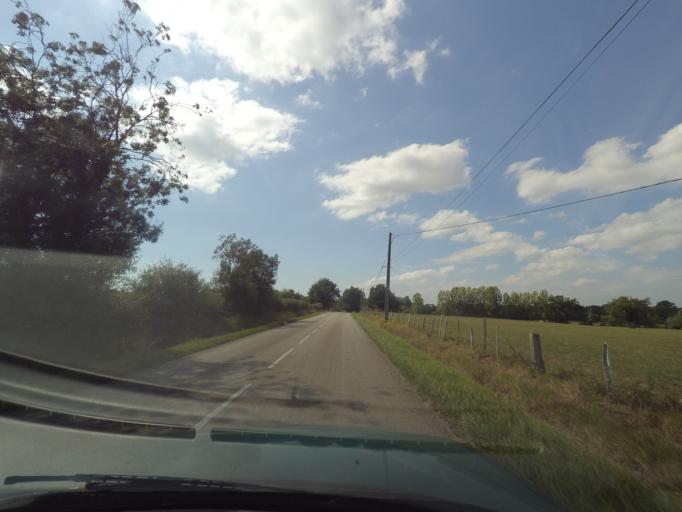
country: FR
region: Pays de la Loire
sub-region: Departement de la Loire-Atlantique
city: Saint-Hilaire-de-Chaleons
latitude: 47.0992
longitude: -1.8501
